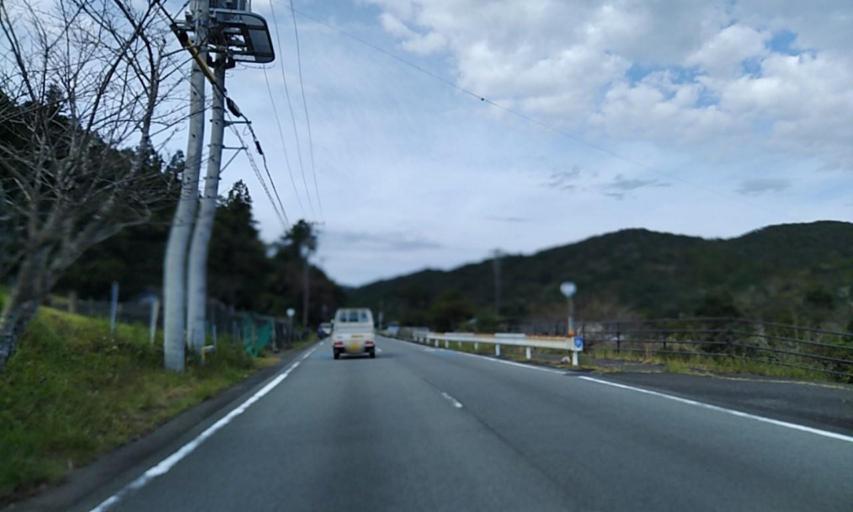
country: JP
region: Mie
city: Ise
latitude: 34.2992
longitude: 136.6387
